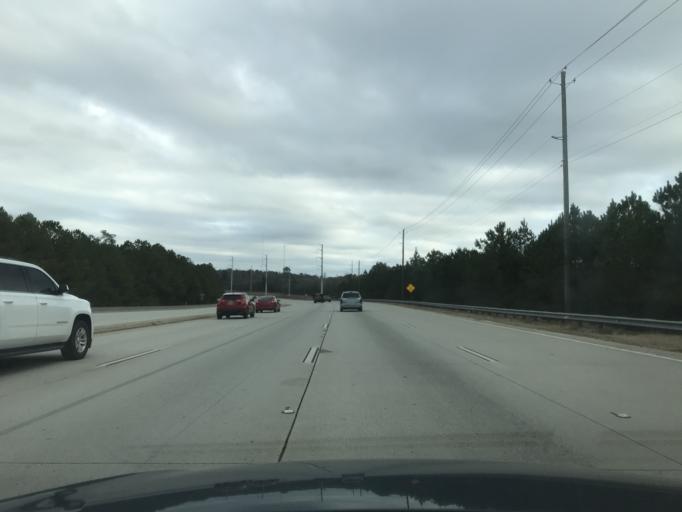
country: US
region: Georgia
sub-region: Columbia County
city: Grovetown
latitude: 33.4394
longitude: -82.1155
